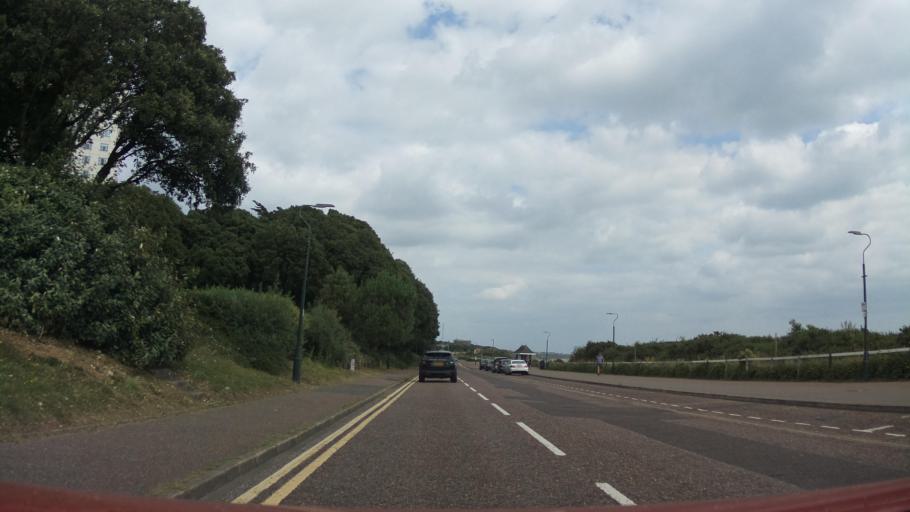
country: GB
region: England
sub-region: Bournemouth
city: Bournemouth
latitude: 50.7194
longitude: -1.8565
